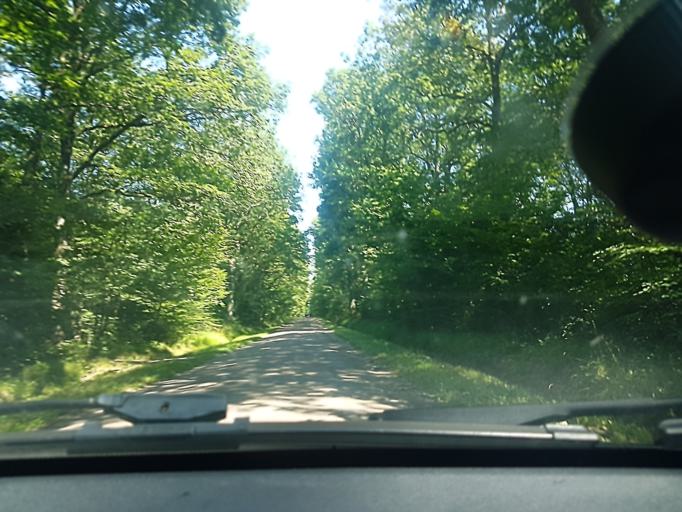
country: FR
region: Bourgogne
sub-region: Departement de Saone-et-Loire
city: Fontaines
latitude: 46.8903
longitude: 4.7978
